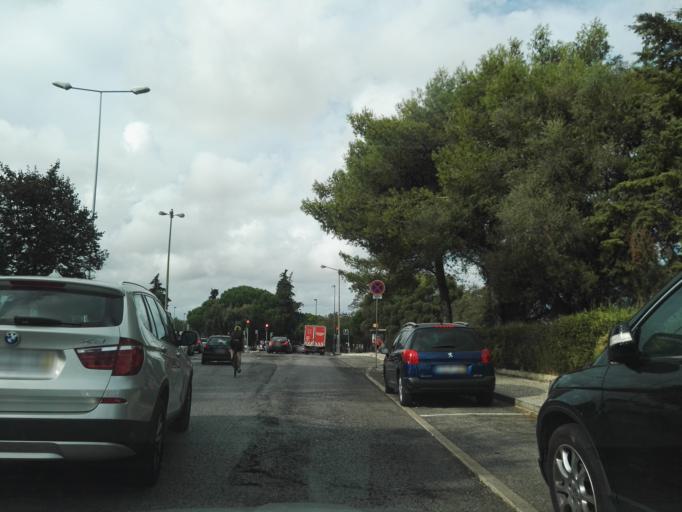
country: PT
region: Lisbon
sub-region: Lisbon
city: Lisbon
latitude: 38.7496
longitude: -9.1580
